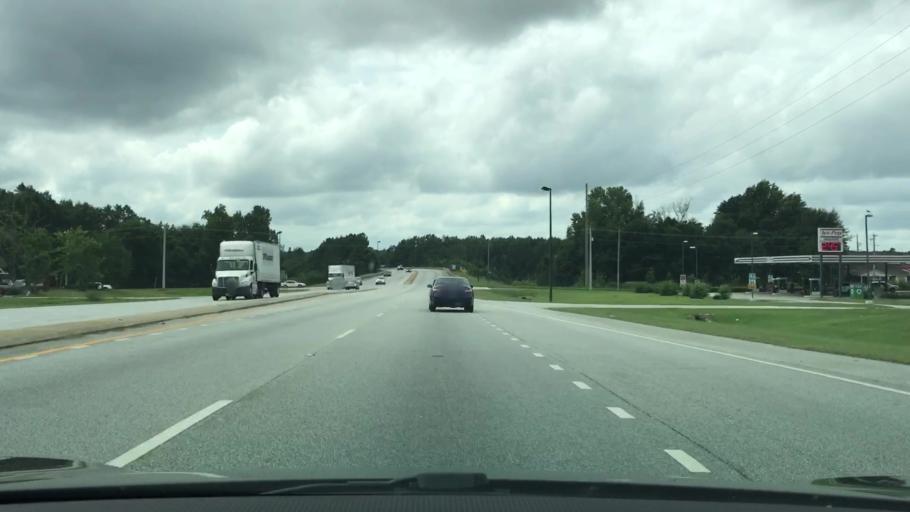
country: US
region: Alabama
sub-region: Lee County
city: Opelika
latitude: 32.6366
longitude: -85.4097
